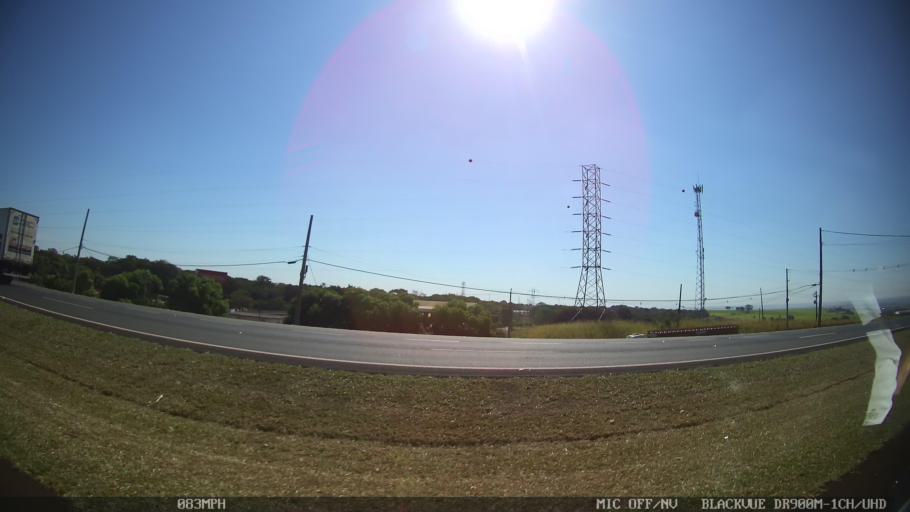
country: BR
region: Sao Paulo
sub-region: Ribeirao Preto
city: Ribeirao Preto
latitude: -21.1457
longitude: -47.8767
